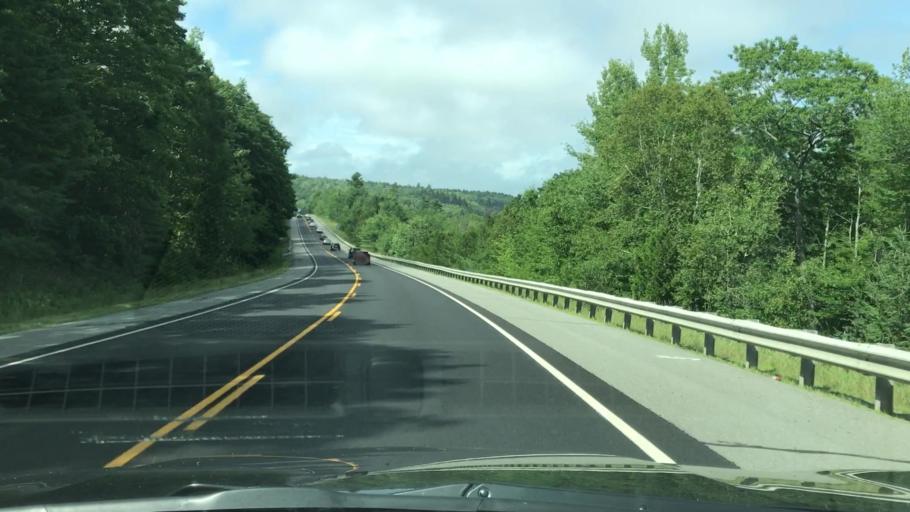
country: US
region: Maine
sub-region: Hancock County
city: Bucksport
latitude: 44.5463
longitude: -68.8090
